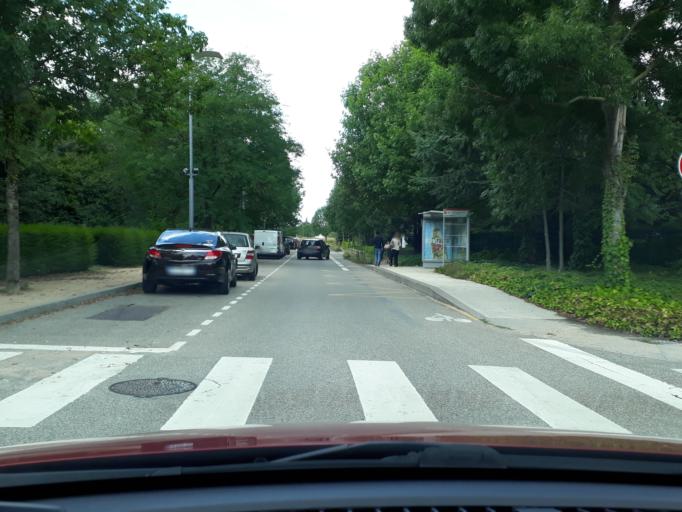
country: FR
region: Rhone-Alpes
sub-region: Departement du Rhone
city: Saint-Priest
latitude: 45.7147
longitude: 4.9322
